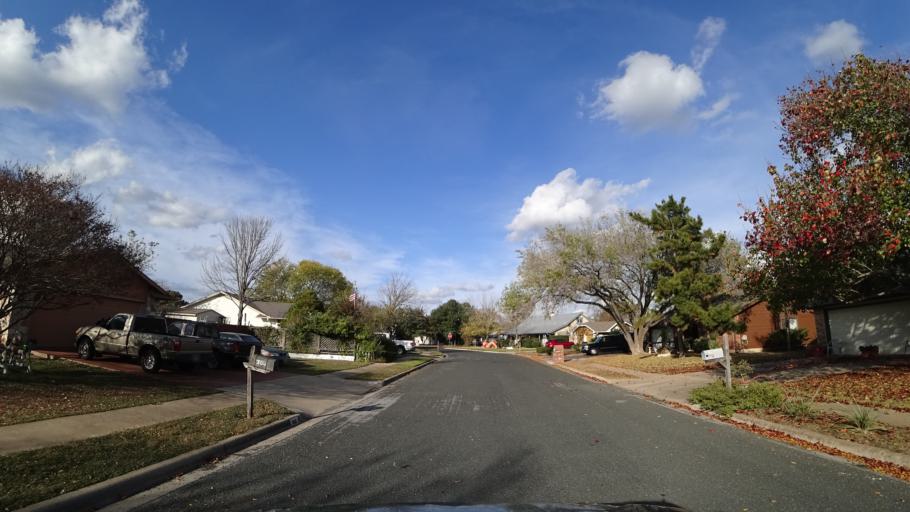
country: US
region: Texas
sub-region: Williamson County
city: Brushy Creek
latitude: 30.5096
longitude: -97.7294
